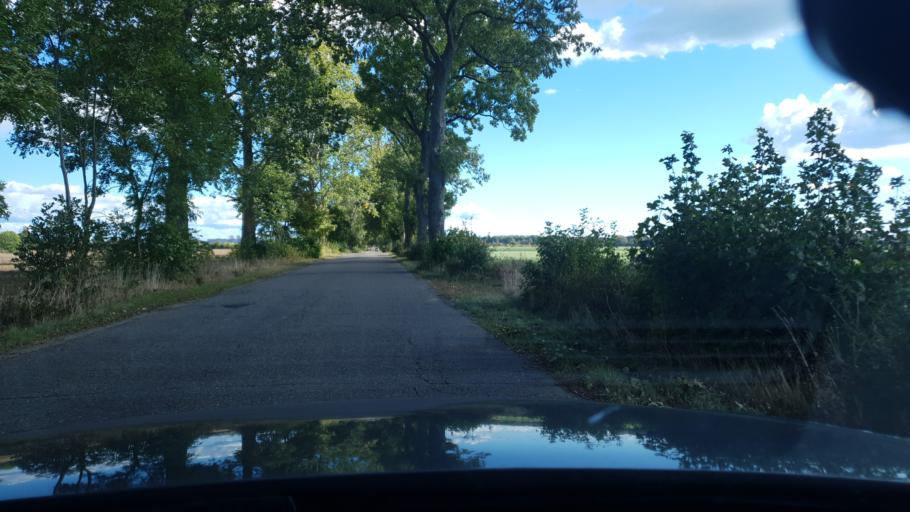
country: PL
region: Pomeranian Voivodeship
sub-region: Powiat pucki
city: Zelistrzewo
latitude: 54.6876
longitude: 18.4387
